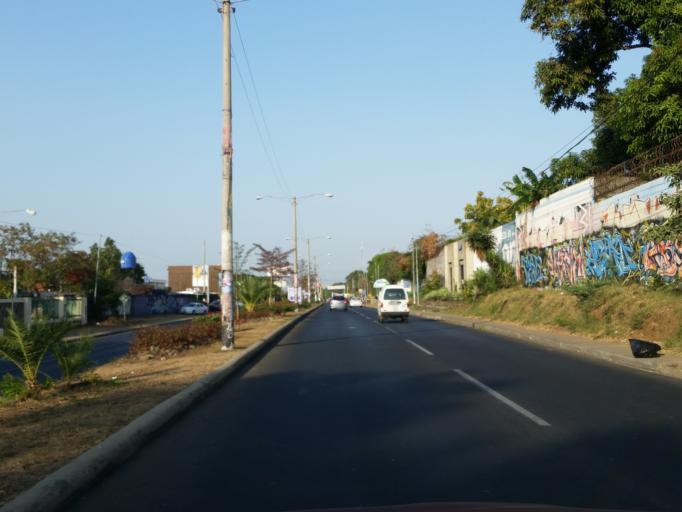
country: NI
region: Managua
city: Managua
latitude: 12.1245
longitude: -86.2599
